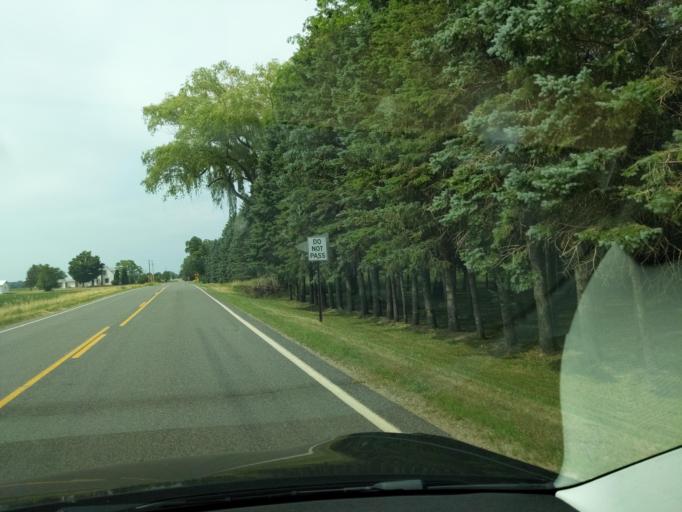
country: US
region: Michigan
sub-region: Clinton County
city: Saint Johns
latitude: 42.9259
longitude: -84.6020
